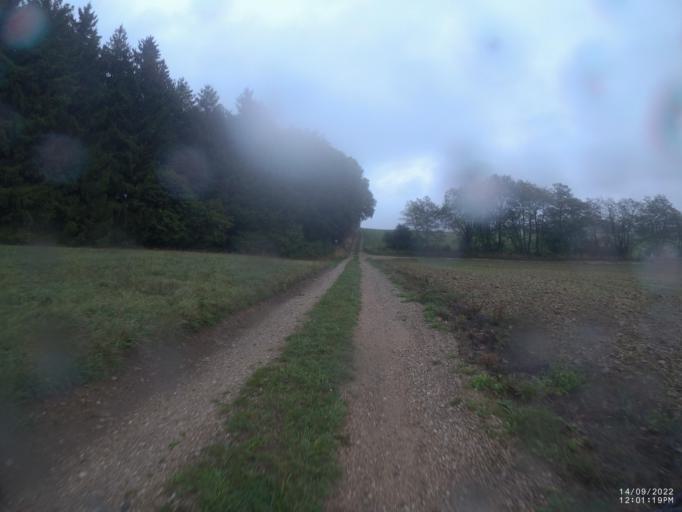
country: DE
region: Rheinland-Pfalz
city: Uxheim
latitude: 50.3304
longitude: 6.7284
